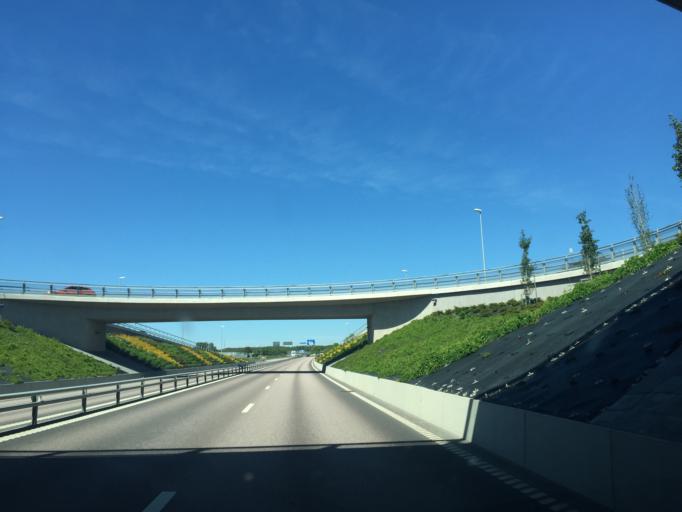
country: SE
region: OEstergoetland
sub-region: Motala Kommun
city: Motala
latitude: 58.5449
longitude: 15.0157
